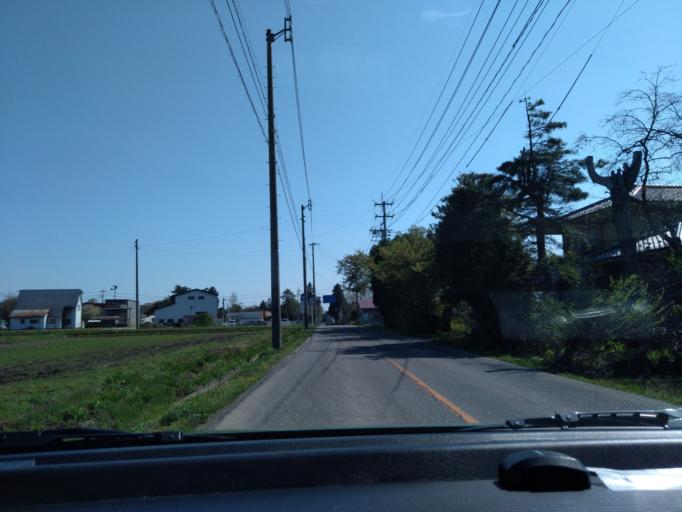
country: JP
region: Akita
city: Omagari
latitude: 39.4685
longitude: 140.5833
